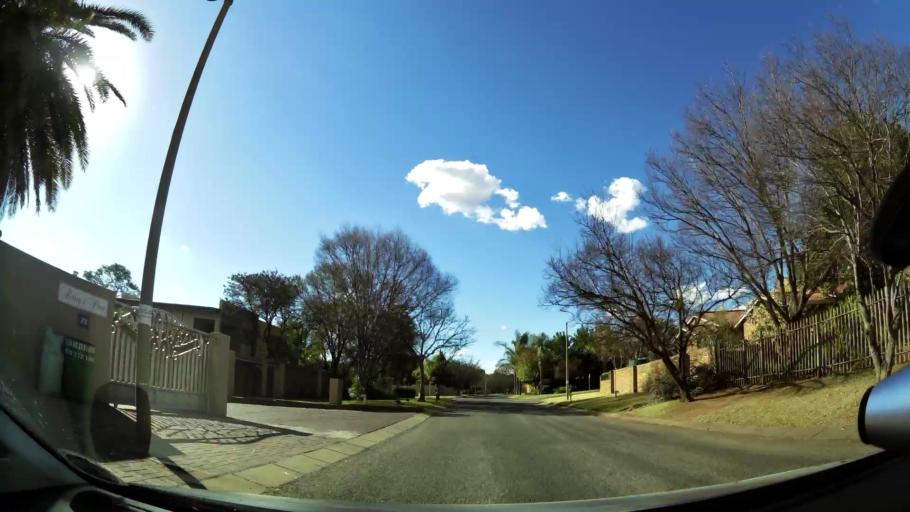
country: ZA
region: North-West
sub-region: Dr Kenneth Kaunda District Municipality
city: Klerksdorp
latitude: -26.8281
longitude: 26.6751
